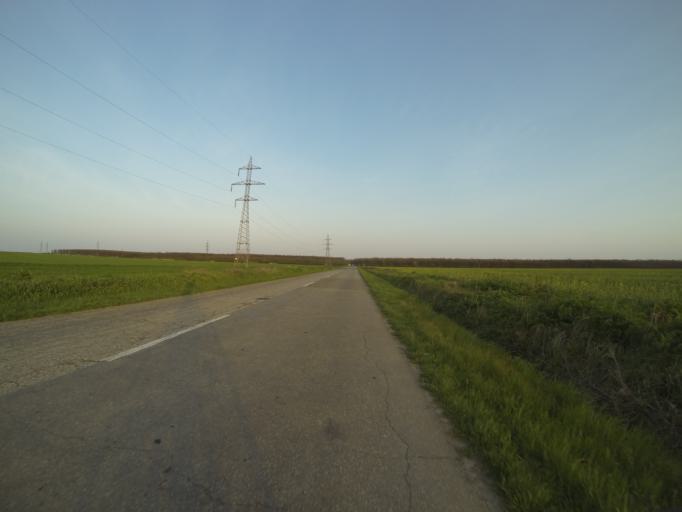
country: RO
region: Dolj
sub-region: Comuna Dranicu
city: Dranic
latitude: 44.0699
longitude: 23.7988
